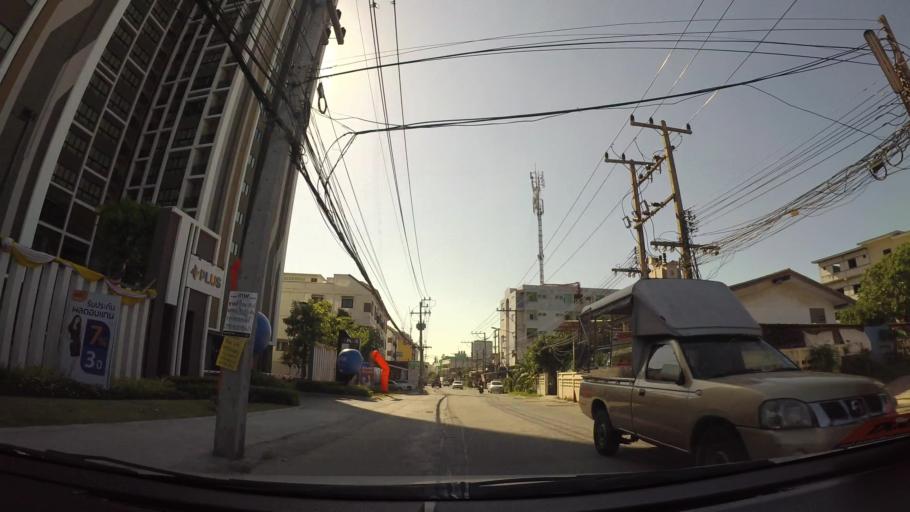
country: TH
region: Chon Buri
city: Si Racha
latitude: 13.1623
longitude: 100.9388
